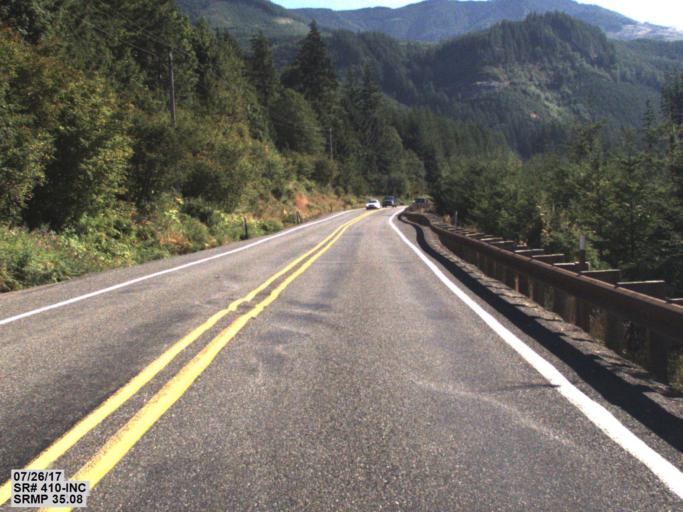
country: US
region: Washington
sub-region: King County
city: Enumclaw
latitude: 47.1712
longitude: -121.8040
